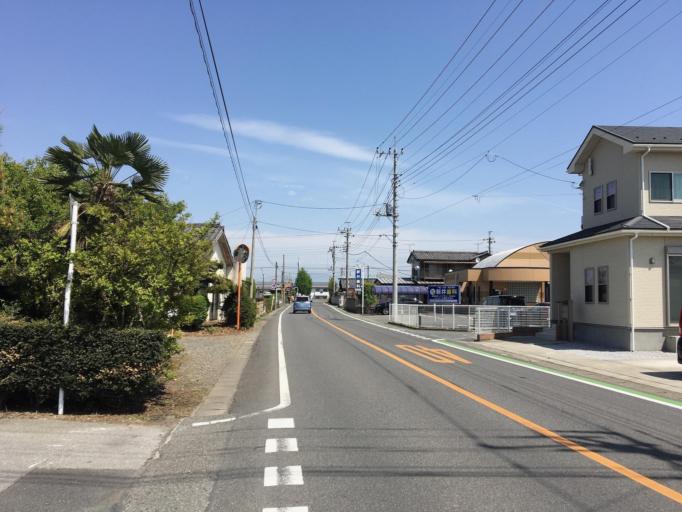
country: JP
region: Gunma
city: Sakai-nakajima
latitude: 36.2745
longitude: 139.2658
